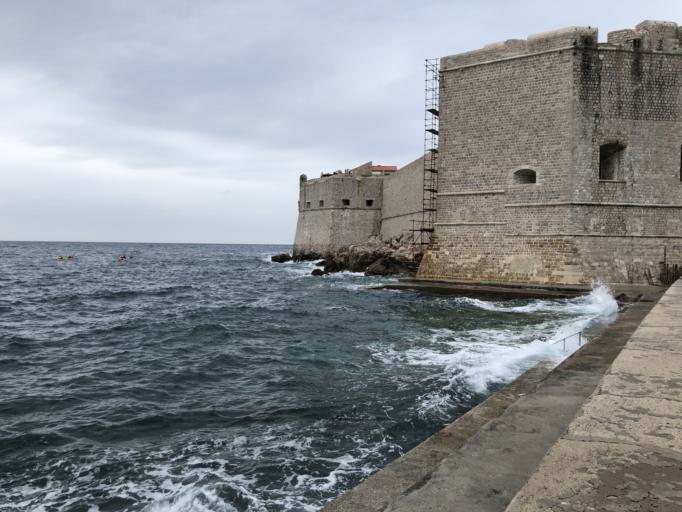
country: HR
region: Dubrovacko-Neretvanska
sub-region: Grad Dubrovnik
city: Dubrovnik
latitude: 42.6398
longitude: 18.1132
